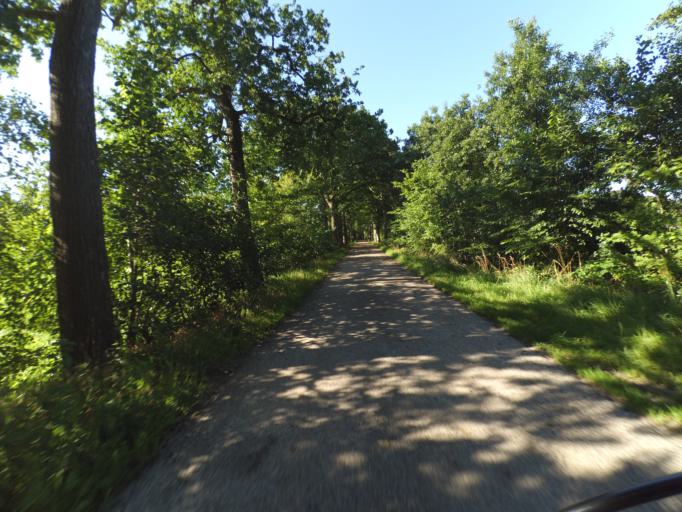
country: NL
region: Friesland
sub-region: Gemeente Achtkarspelen
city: Buitenpost
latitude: 53.2670
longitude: 6.1145
